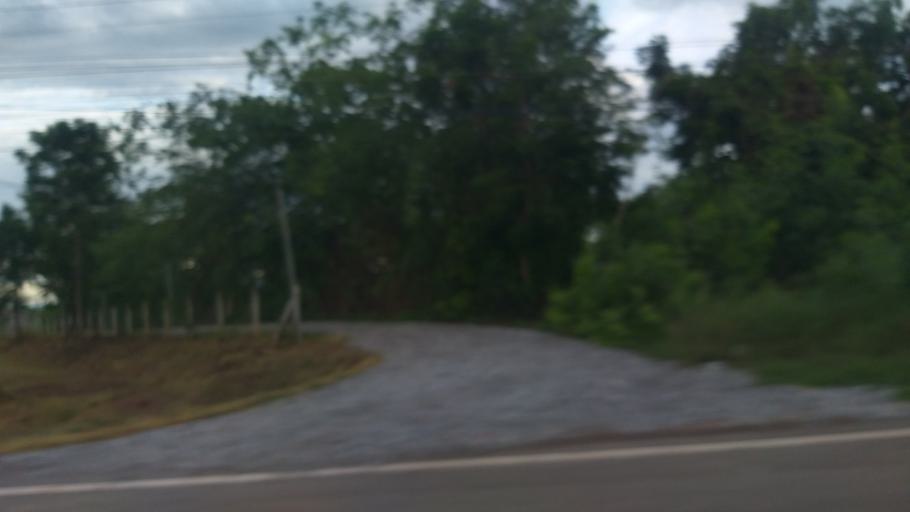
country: TH
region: Chaiyaphum
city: Kaeng Khro
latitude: 16.1880
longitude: 102.2111
